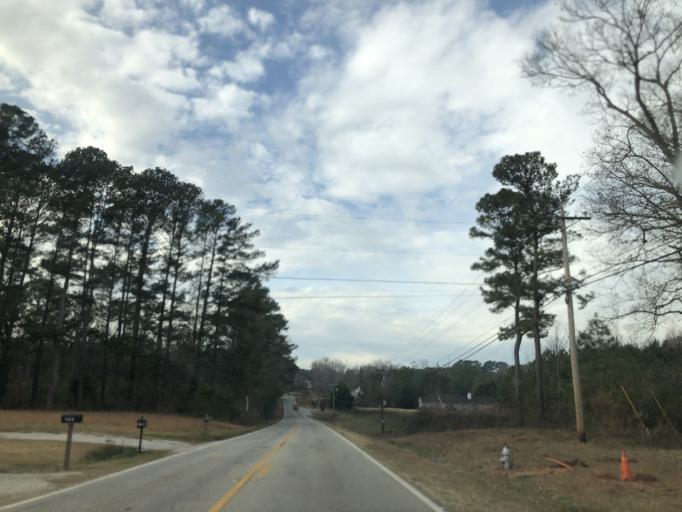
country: US
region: Georgia
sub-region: Henry County
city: Stockbridge
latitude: 33.6069
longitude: -84.2001
